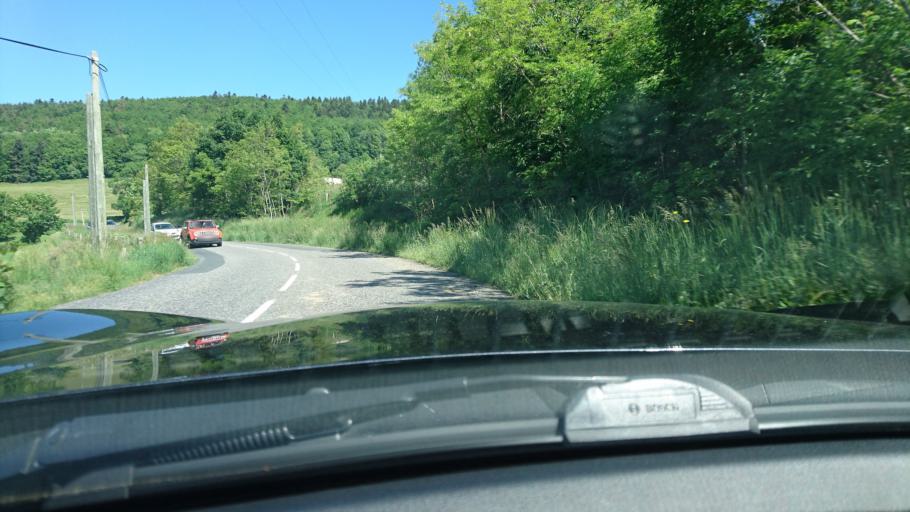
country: FR
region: Rhone-Alpes
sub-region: Departement de la Loire
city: Violay
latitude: 45.8193
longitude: 4.3995
